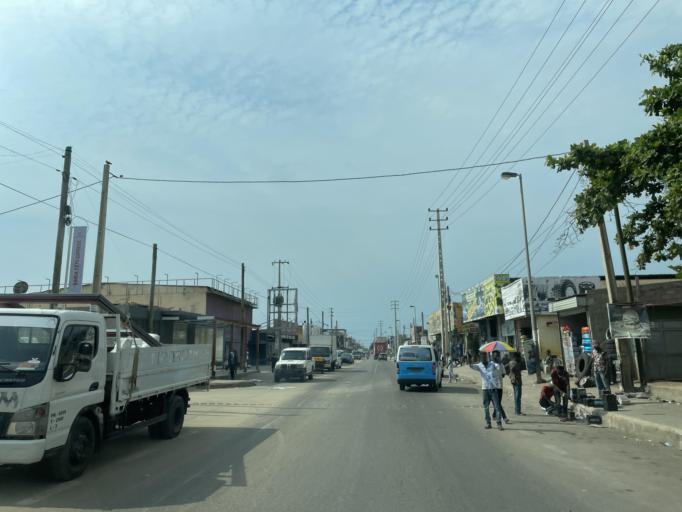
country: AO
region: Luanda
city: Luanda
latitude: -8.9022
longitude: 13.1881
